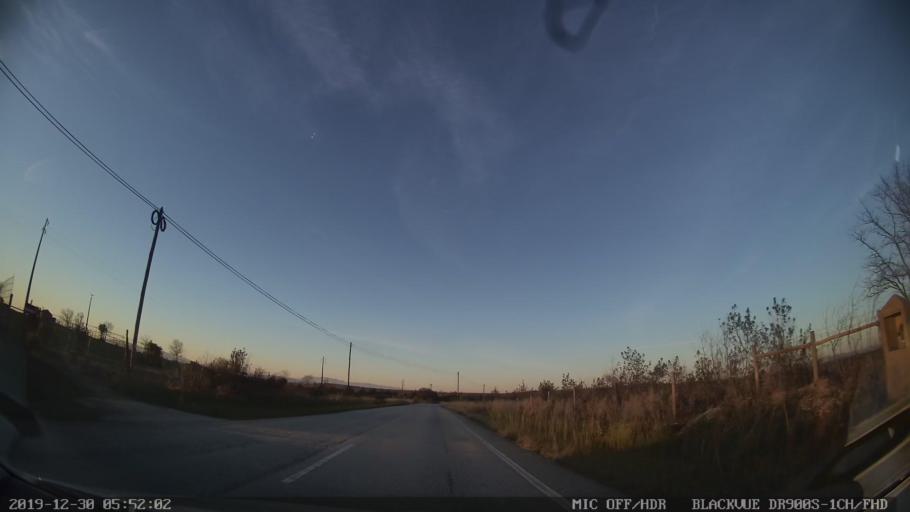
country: PT
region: Castelo Branco
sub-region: Idanha-A-Nova
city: Idanha-a-Nova
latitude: 40.0013
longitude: -7.2476
